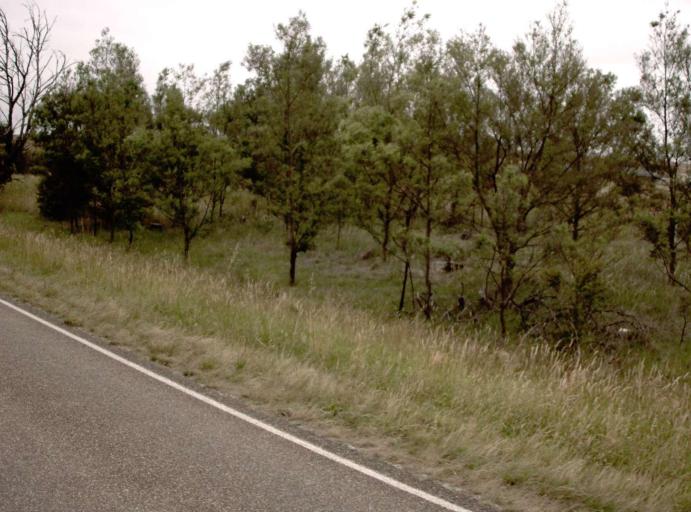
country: AU
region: Victoria
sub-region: Wellington
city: Heyfield
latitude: -38.1335
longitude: 146.7901
